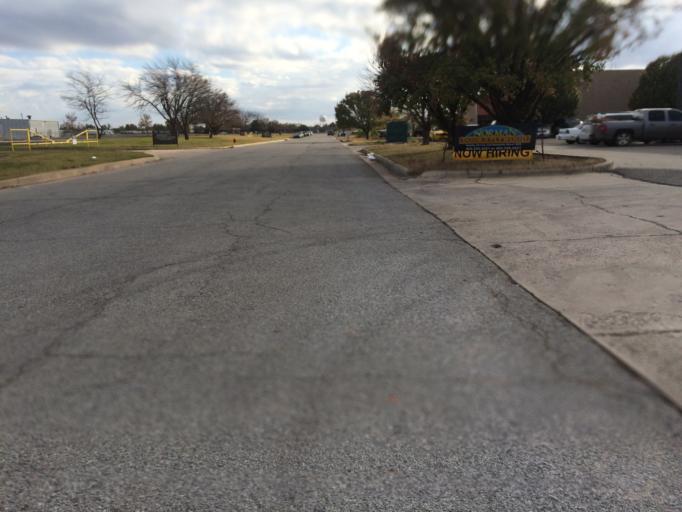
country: US
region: Oklahoma
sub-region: Cleveland County
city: Norman
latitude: 35.2471
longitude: -97.4529
